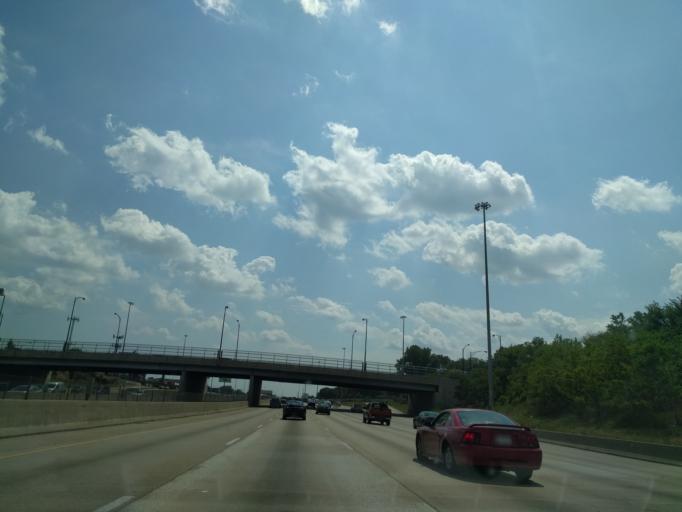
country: US
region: Illinois
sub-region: Cook County
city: Evergreen Park
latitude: 41.7574
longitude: -87.6257
